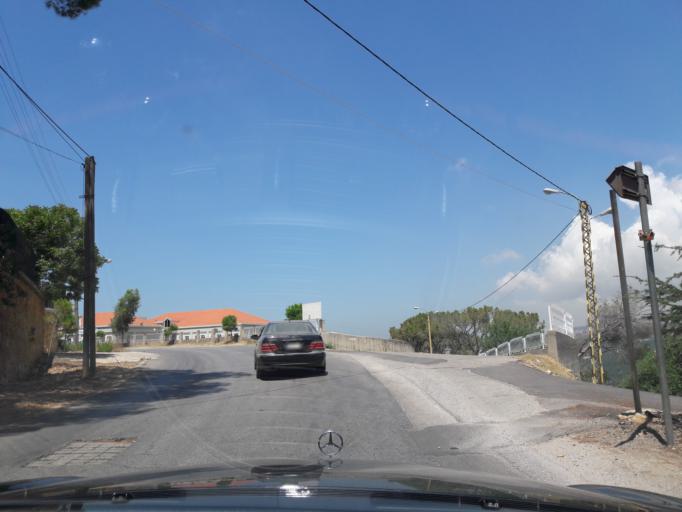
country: LB
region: Mont-Liban
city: Djounie
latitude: 33.9265
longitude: 35.6628
